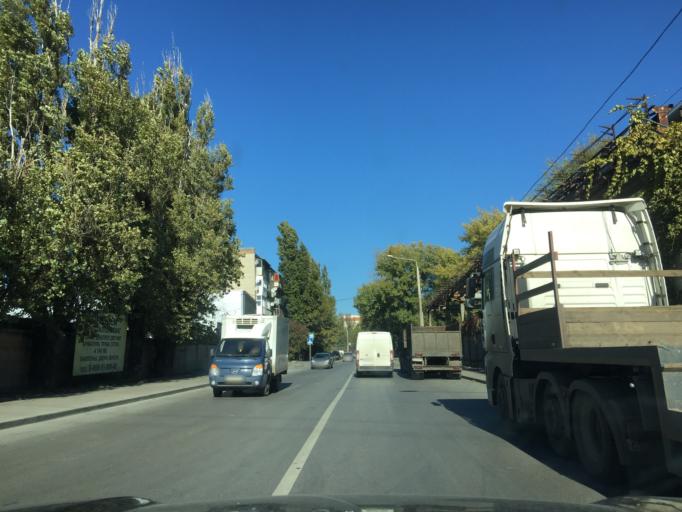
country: RU
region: Rostov
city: Imeni Chkalova
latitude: 47.2599
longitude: 39.7544
